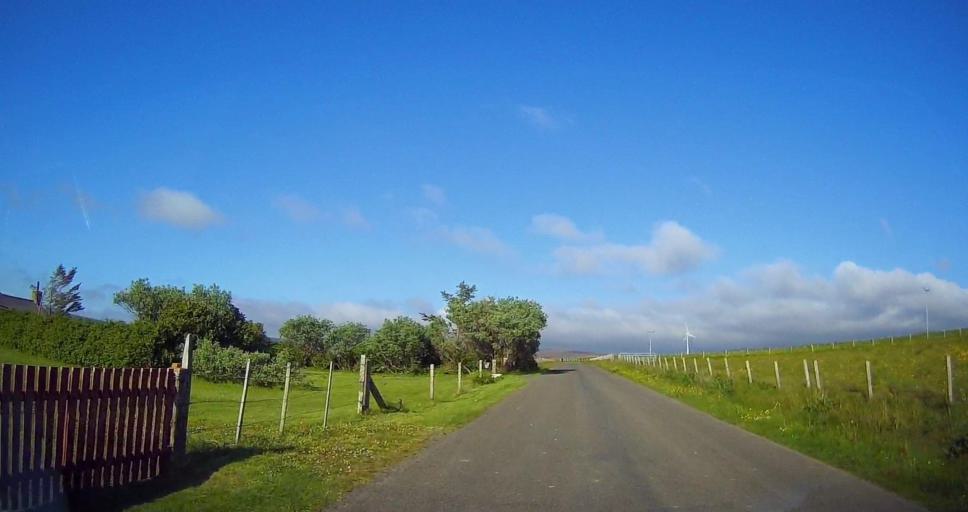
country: GB
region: Scotland
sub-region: Orkney Islands
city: Stromness
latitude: 59.0742
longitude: -3.2087
